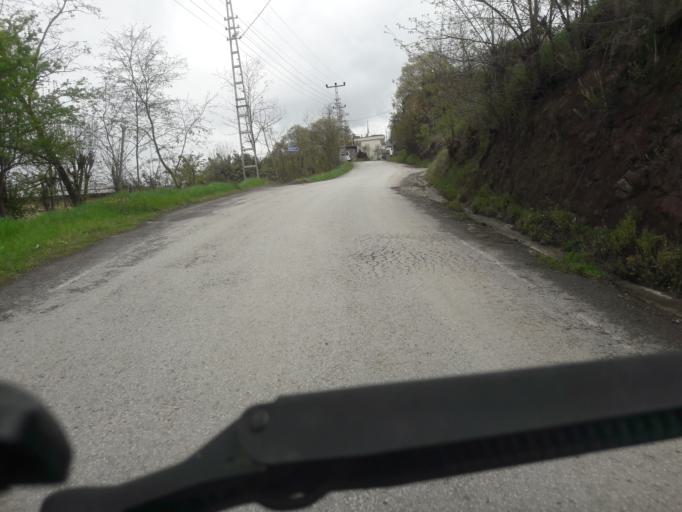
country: TR
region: Trabzon
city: Derecik
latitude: 40.9444
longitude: 39.4966
